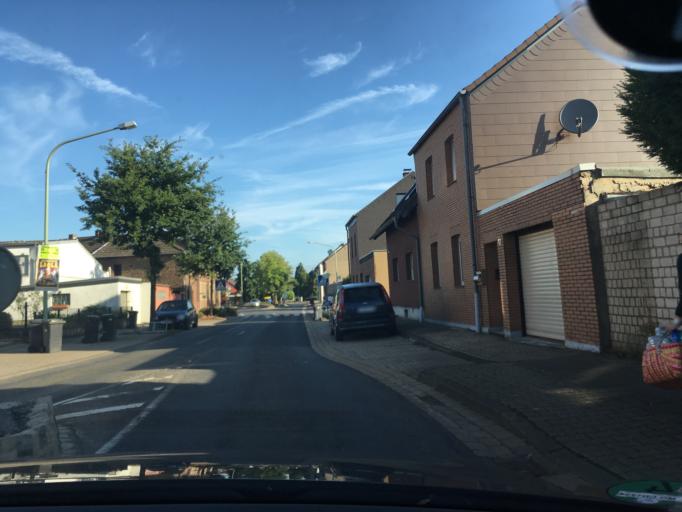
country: DE
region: North Rhine-Westphalia
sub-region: Regierungsbezirk Koln
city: Niederzier
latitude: 50.8662
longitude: 6.4756
